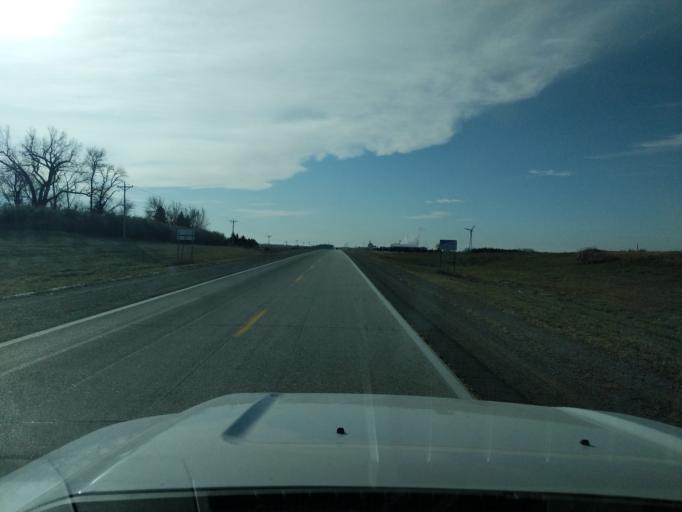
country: US
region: Minnesota
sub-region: Yellow Medicine County
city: Granite Falls
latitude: 44.8309
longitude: -95.4836
